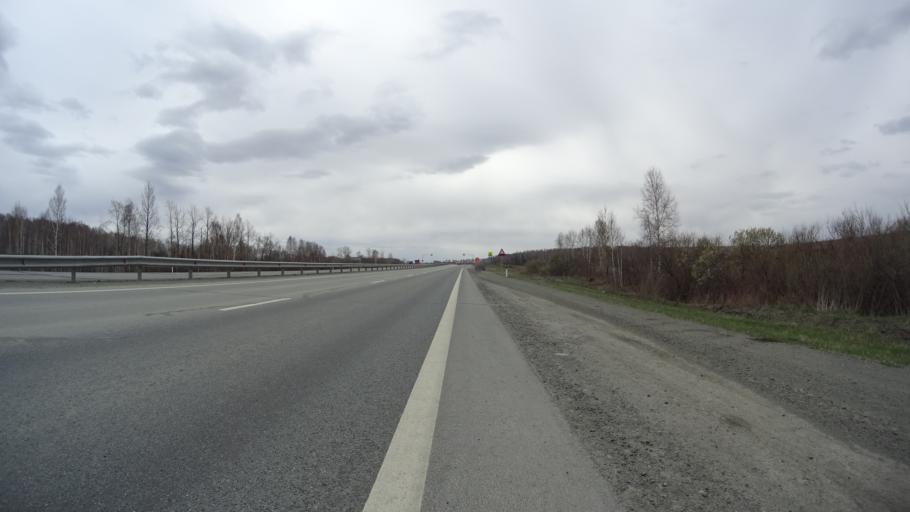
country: RU
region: Chelyabinsk
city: Yemanzhelinka
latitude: 54.8262
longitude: 61.3102
